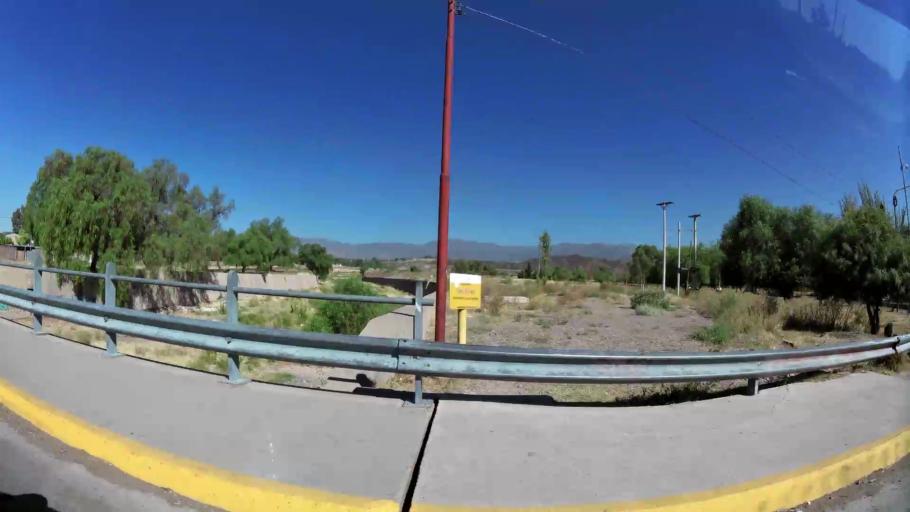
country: AR
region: Mendoza
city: Mendoza
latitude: -32.8999
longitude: -68.8769
